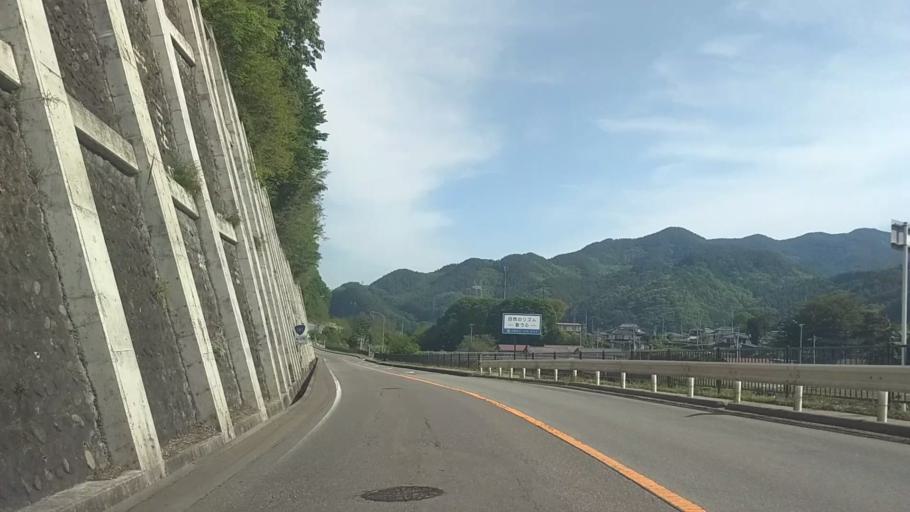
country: JP
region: Nagano
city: Saku
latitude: 36.0986
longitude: 138.4824
